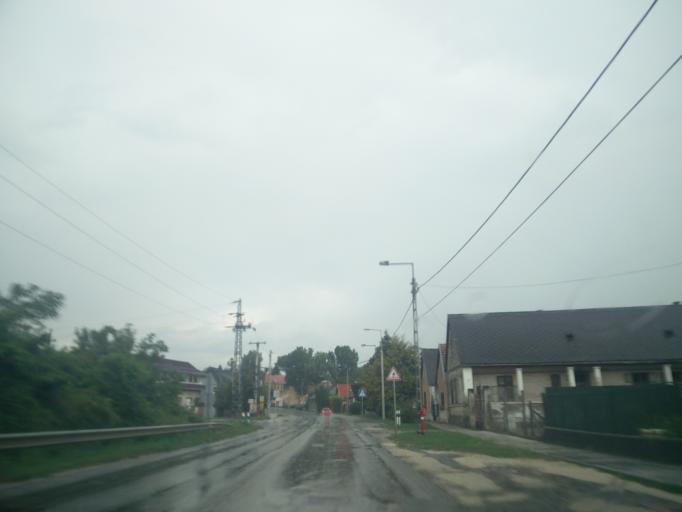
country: HU
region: Pest
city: Biatorbagy
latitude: 47.4597
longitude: 18.8112
